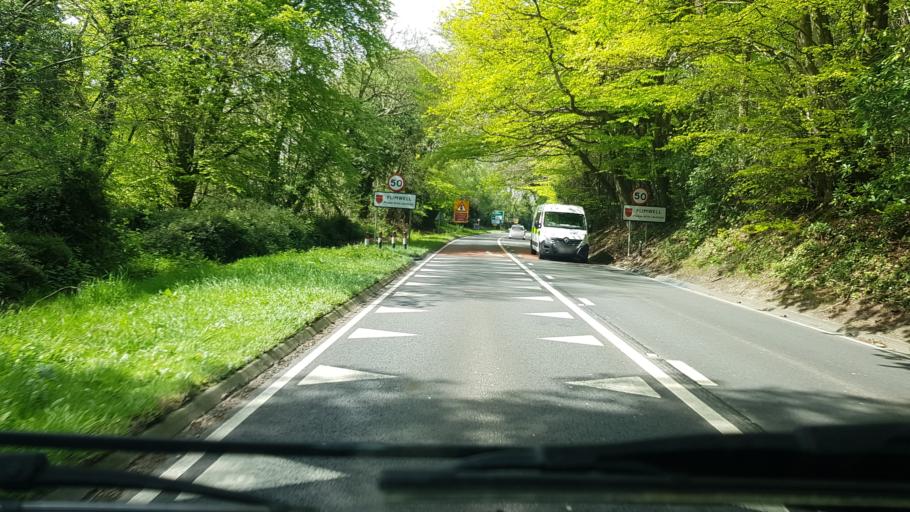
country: GB
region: England
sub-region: Kent
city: Hawkhurst
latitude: 51.0525
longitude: 0.4481
